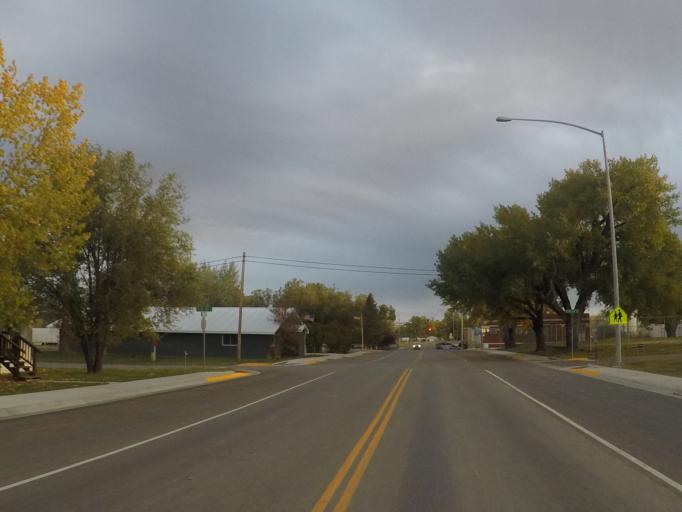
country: US
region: Montana
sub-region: Golden Valley County
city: Ryegate
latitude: 46.2994
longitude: -109.2563
